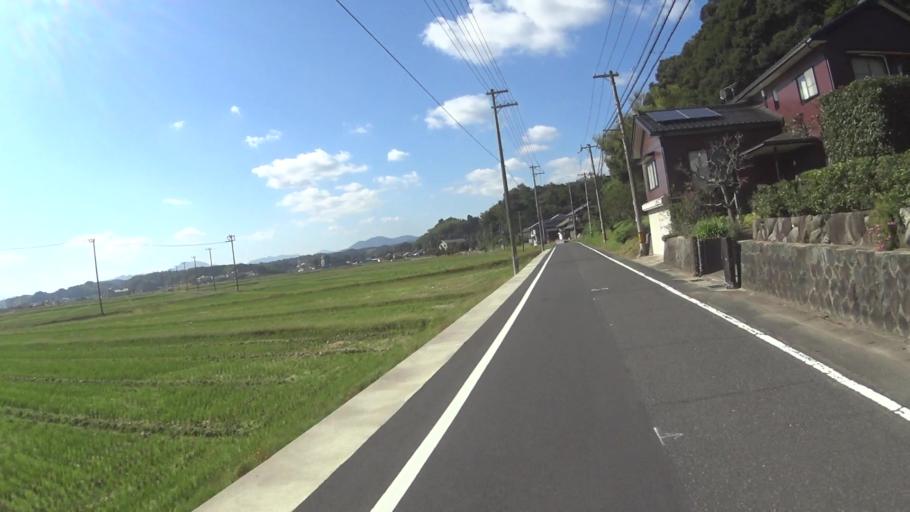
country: JP
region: Kyoto
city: Miyazu
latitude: 35.6795
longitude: 135.0872
